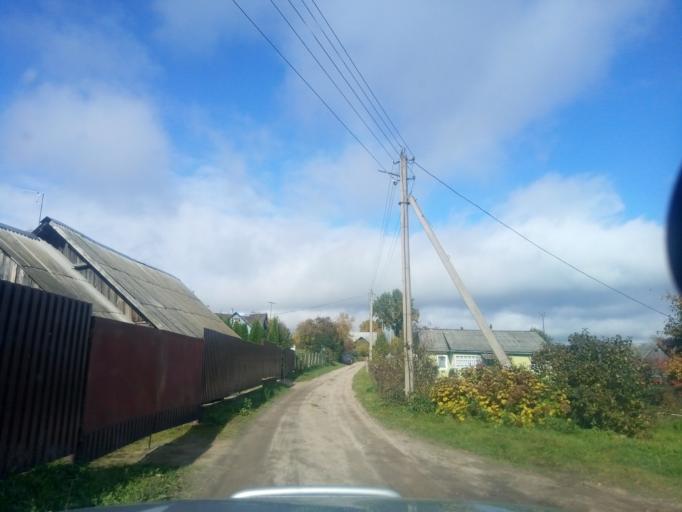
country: BY
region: Minsk
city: Zaslawye
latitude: 54.0232
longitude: 27.2869
